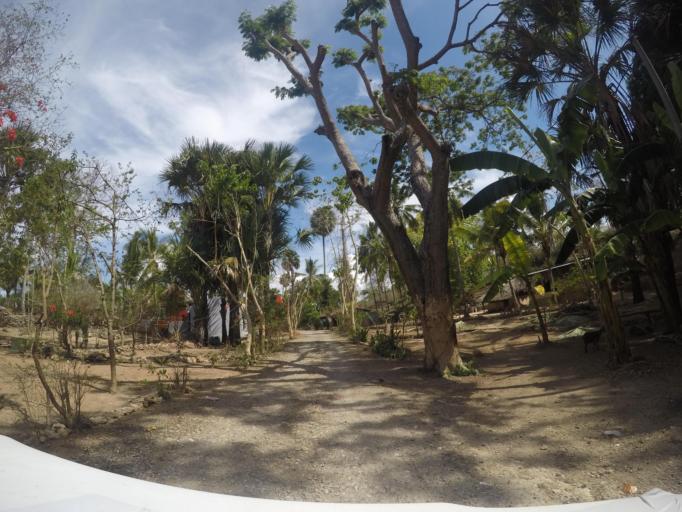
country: TL
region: Baucau
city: Baucau
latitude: -8.4692
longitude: 126.4635
